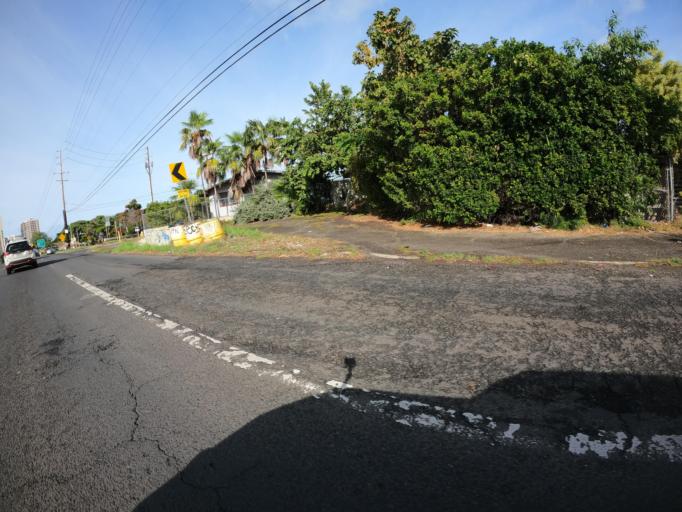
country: US
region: Hawaii
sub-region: Honolulu County
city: Honolulu
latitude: 21.2908
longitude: -157.8158
